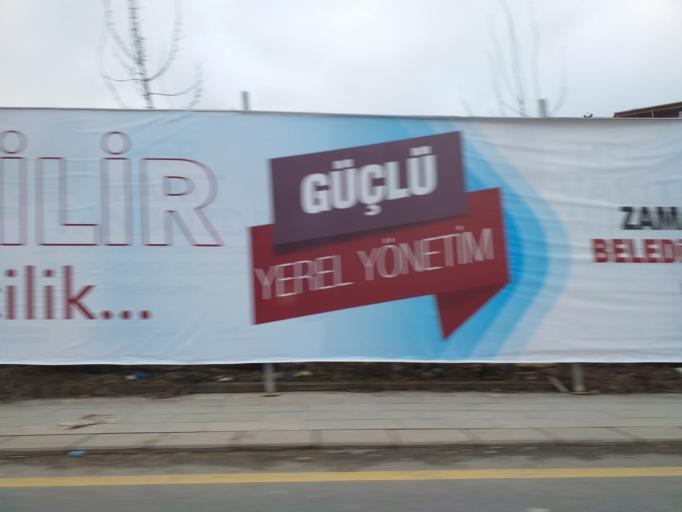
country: TR
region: Ankara
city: Ankara
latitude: 39.9811
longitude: 32.8226
